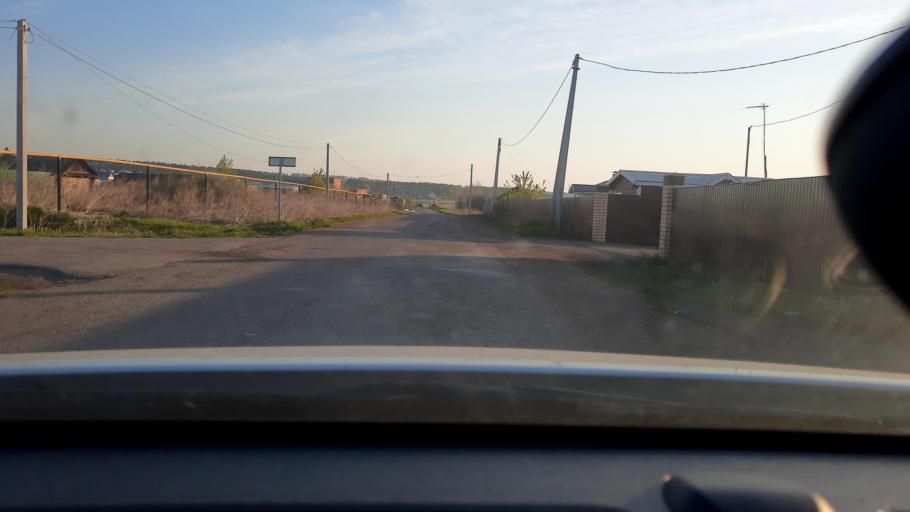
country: RU
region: Bashkortostan
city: Avdon
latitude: 54.5064
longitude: 55.8155
